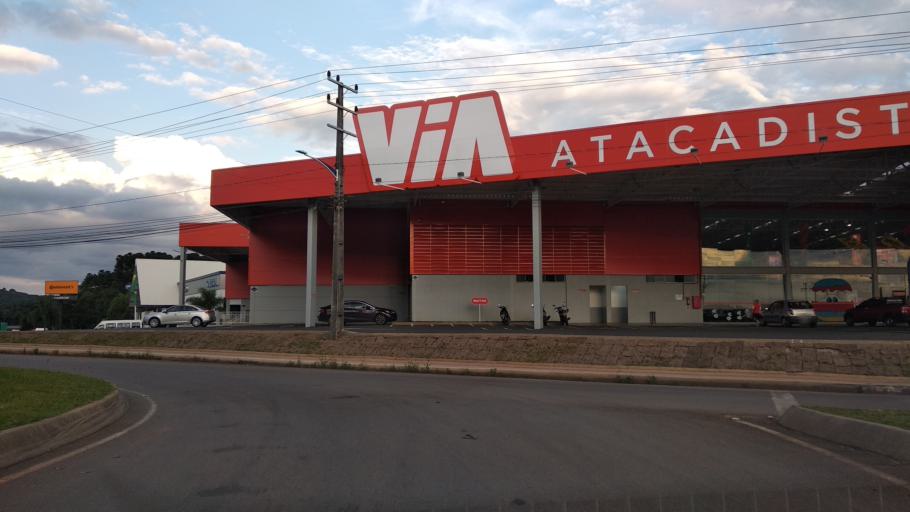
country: BR
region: Santa Catarina
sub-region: Videira
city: Videira
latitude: -26.9986
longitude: -51.1170
